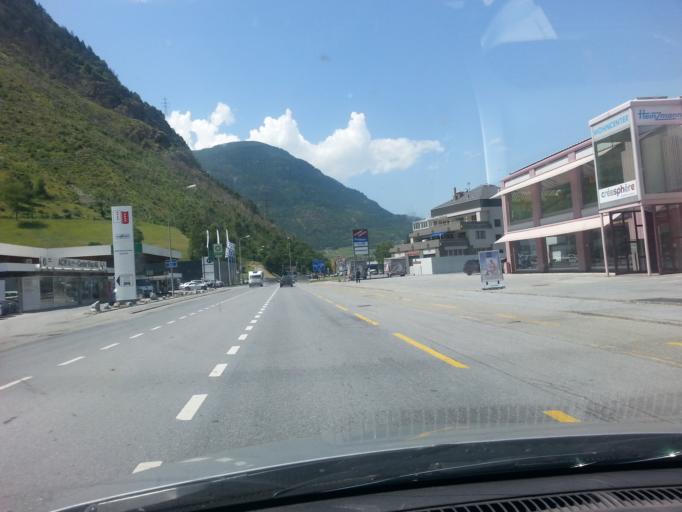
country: CH
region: Valais
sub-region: Visp District
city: Visp
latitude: 46.2944
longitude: 7.9057
